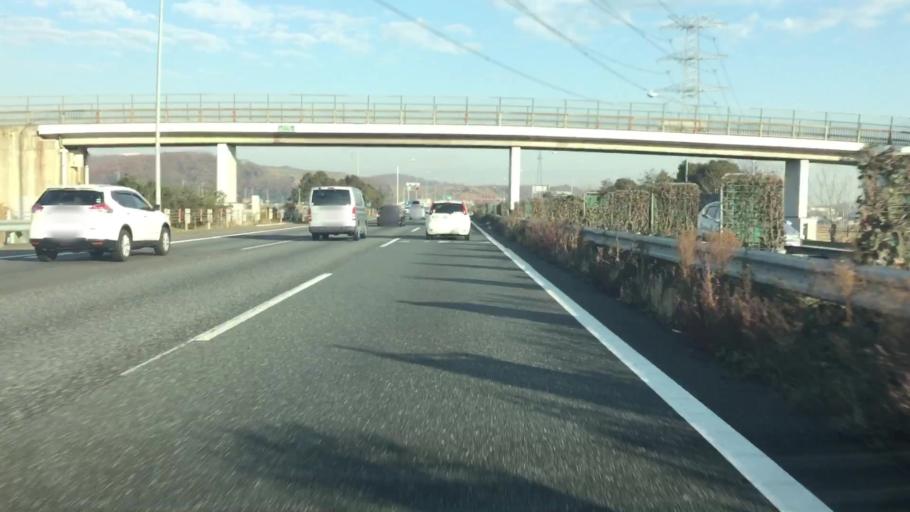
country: JP
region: Saitama
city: Sakado
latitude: 35.9730
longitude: 139.3801
